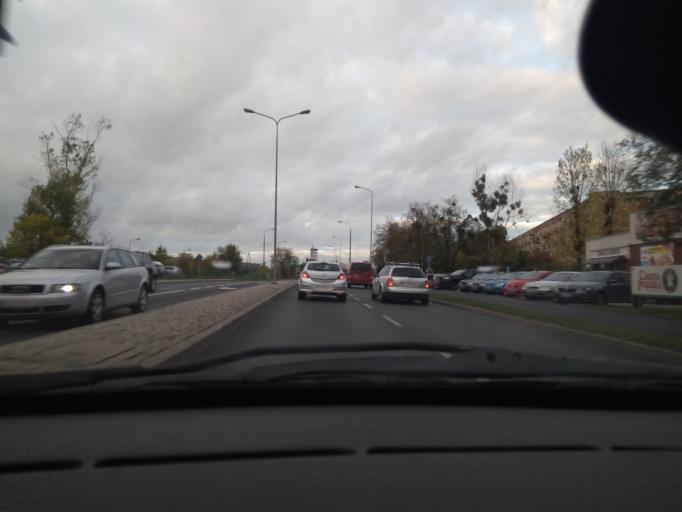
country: PL
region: Greater Poland Voivodeship
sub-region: Poznan
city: Poznan
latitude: 52.4299
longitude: 16.9202
